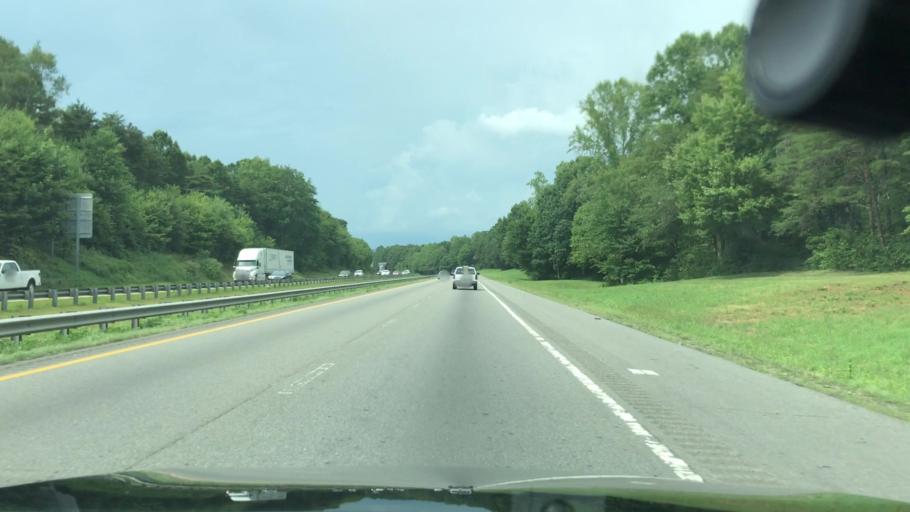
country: US
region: North Carolina
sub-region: Iredell County
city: Mooresville
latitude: 35.6113
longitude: -80.8577
